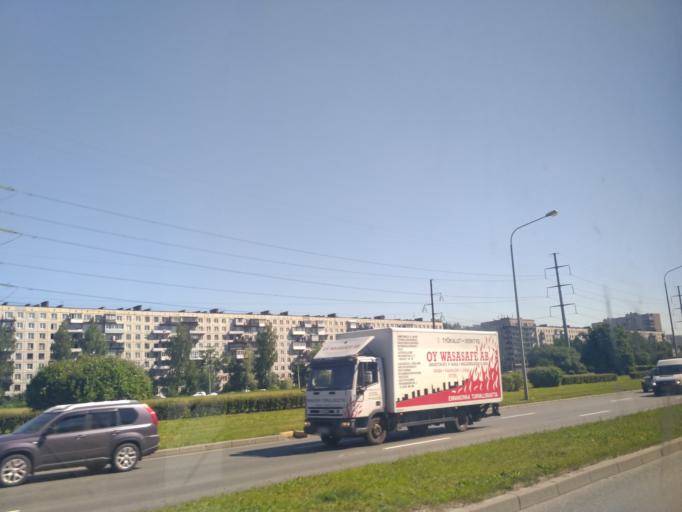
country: RU
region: Leningrad
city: Kalininskiy
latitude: 59.9770
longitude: 30.3983
